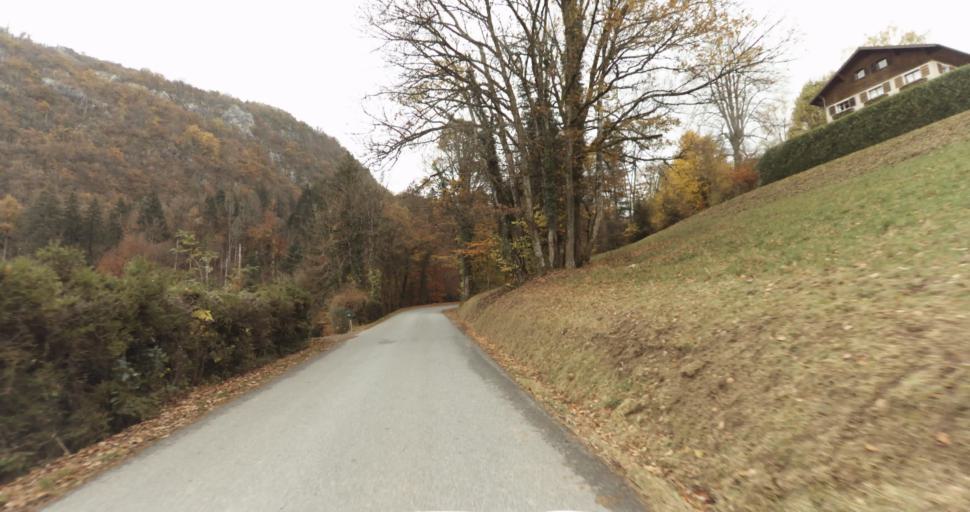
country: FR
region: Rhone-Alpes
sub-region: Departement de la Haute-Savoie
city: Talloires
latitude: 45.8182
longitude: 6.1967
